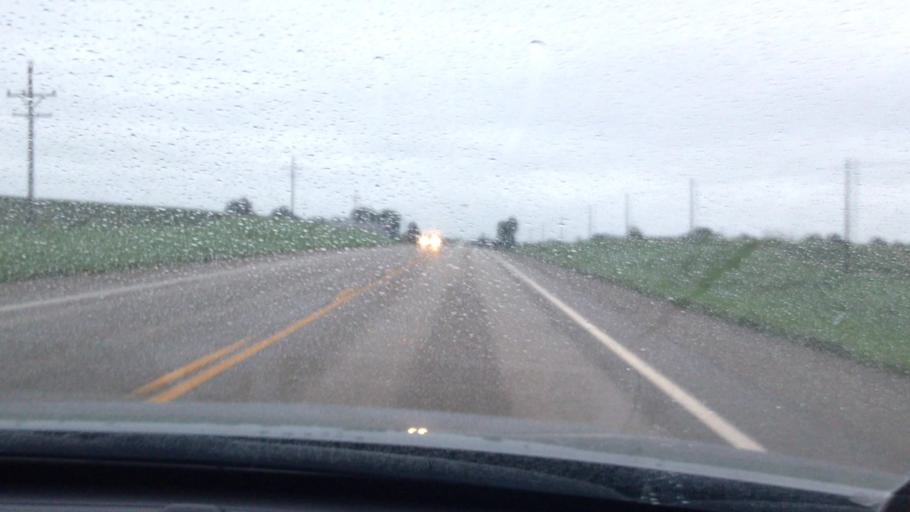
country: US
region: Kansas
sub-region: Brown County
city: Hiawatha
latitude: 39.8086
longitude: -95.5273
